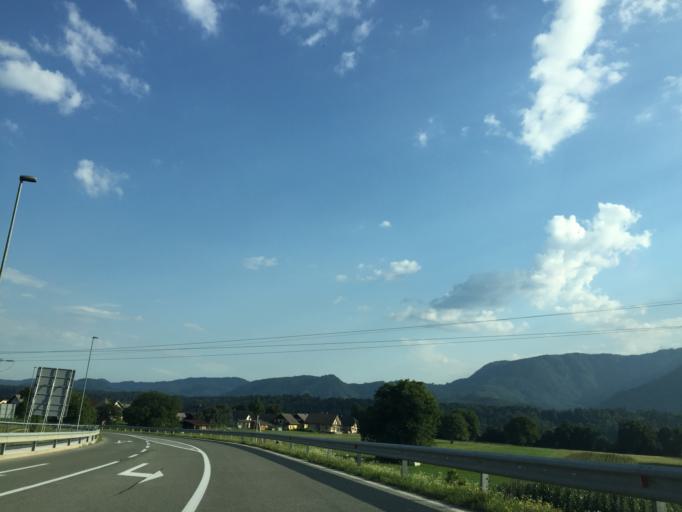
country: SI
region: Radovljica
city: Radovljica
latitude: 46.3253
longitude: 14.2201
